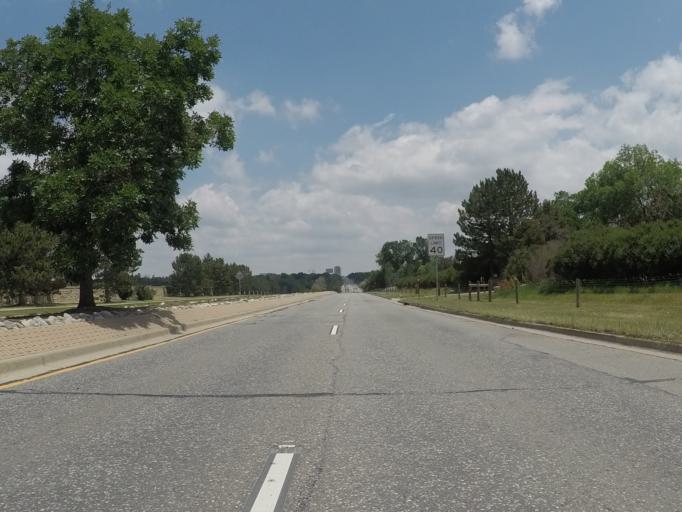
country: US
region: Colorado
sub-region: Arapahoe County
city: Greenwood Village
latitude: 39.6242
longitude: -104.9487
